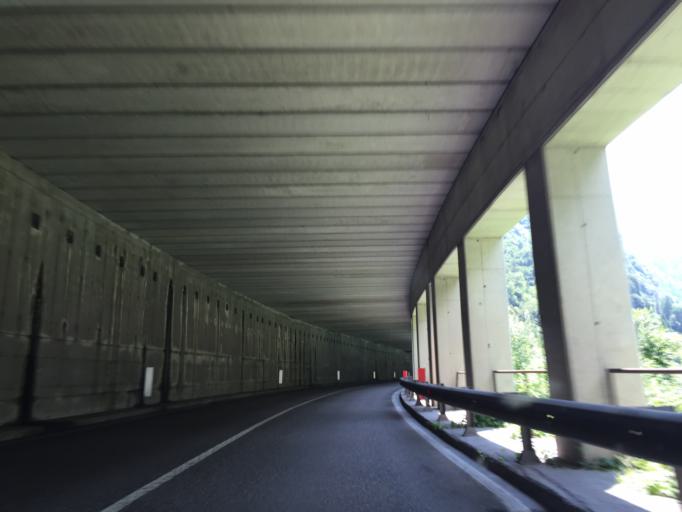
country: IT
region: Trentino-Alto Adige
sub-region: Provincia di Trento
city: Imer
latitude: 46.1205
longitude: 11.7747
